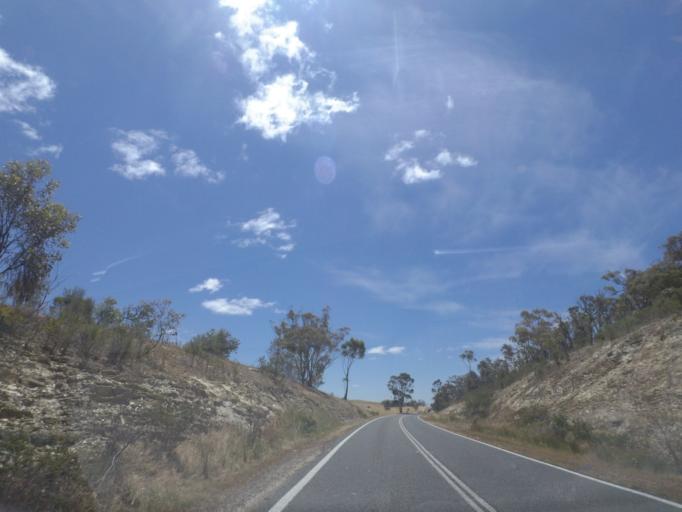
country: AU
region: Victoria
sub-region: Mount Alexander
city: Castlemaine
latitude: -37.2143
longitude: 144.1401
